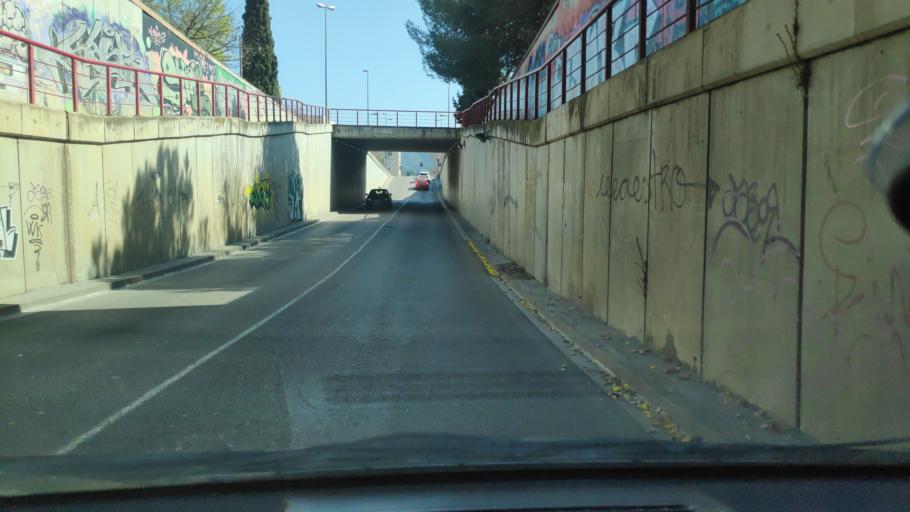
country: ES
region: Catalonia
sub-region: Provincia de Barcelona
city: Mollet del Valles
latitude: 41.5472
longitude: 2.2161
